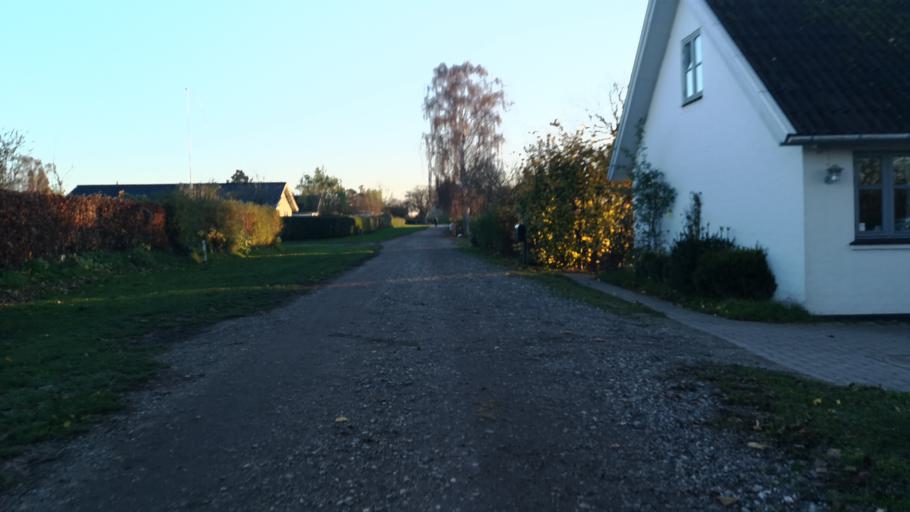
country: DK
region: Capital Region
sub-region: Frederikssund Kommune
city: Slangerup
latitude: 55.8556
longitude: 12.1651
